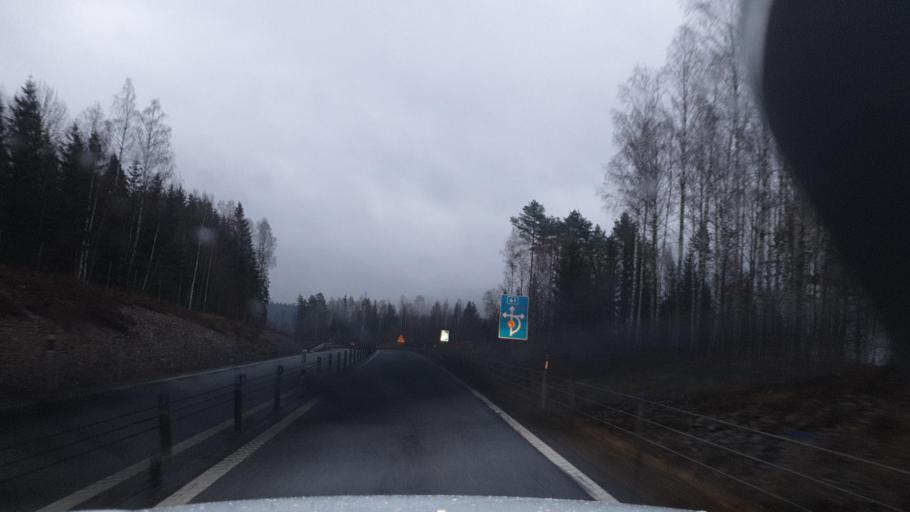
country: SE
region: Vaermland
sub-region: Eda Kommun
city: Amotfors
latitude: 59.7563
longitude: 12.4318
